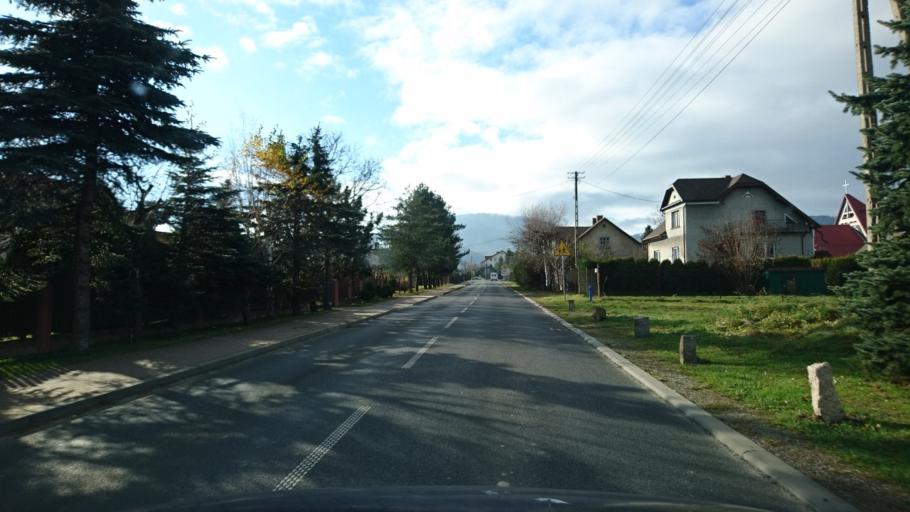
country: PL
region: Silesian Voivodeship
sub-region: Powiat bielski
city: Rybarzowice
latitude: 49.7098
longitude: 19.1078
